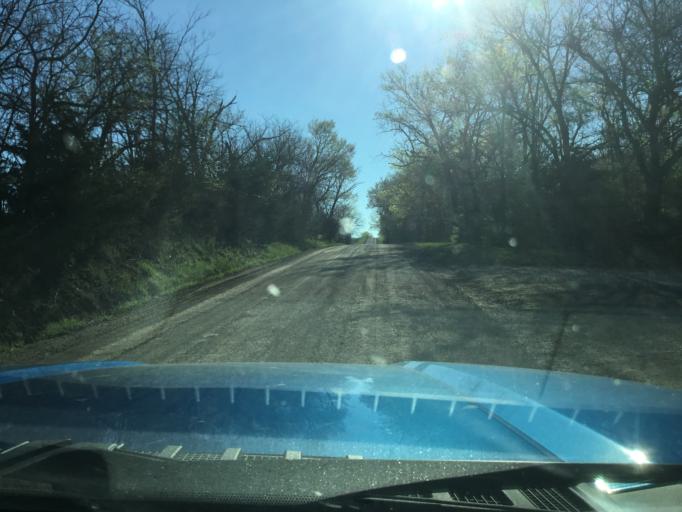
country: US
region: Kansas
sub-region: Douglas County
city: Lawrence
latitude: 38.9569
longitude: -95.3614
